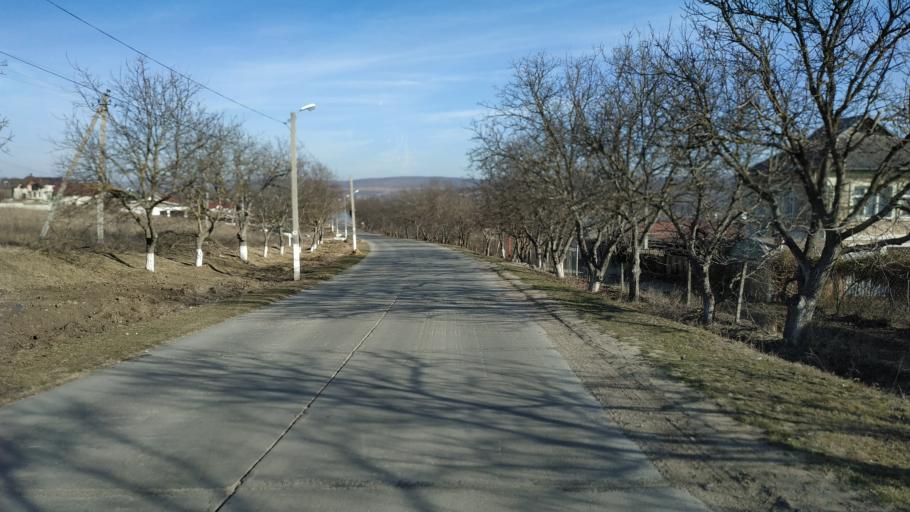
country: MD
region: Chisinau
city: Vatra
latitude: 46.9957
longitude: 28.6742
